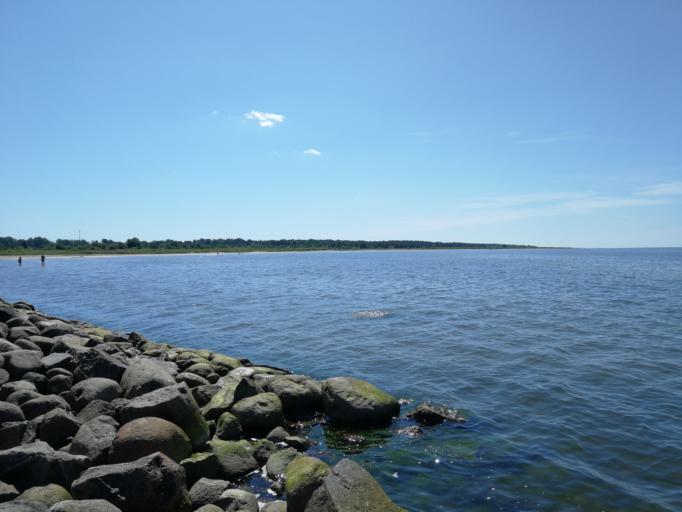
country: LV
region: Salacgrivas
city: Ainazi
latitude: 57.8767
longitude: 24.3489
